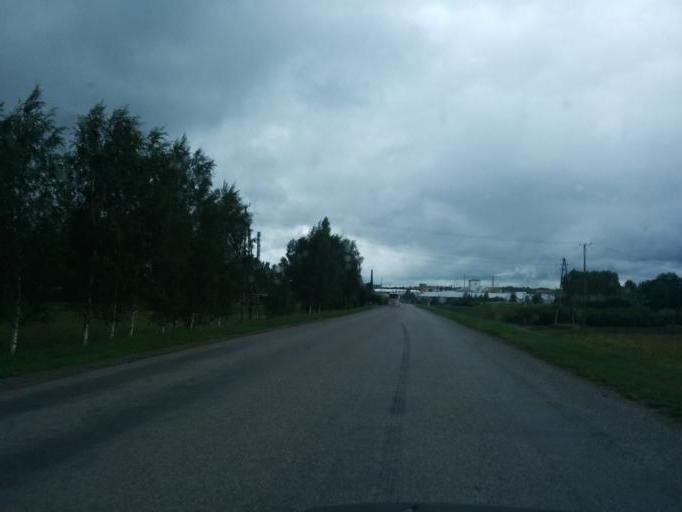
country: LV
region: Valmieras Rajons
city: Valmiera
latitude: 57.5156
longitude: 25.4553
